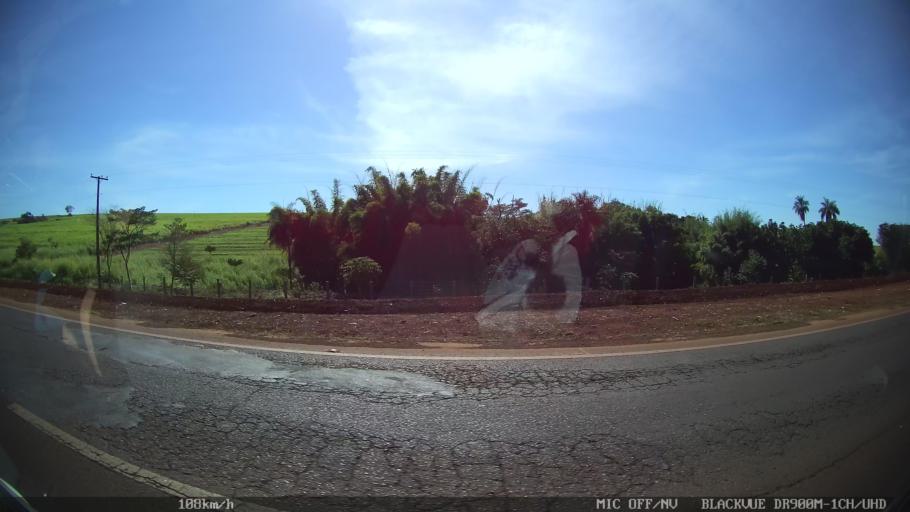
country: BR
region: Sao Paulo
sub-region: Ipua
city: Ipua
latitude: -20.4928
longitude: -48.0170
